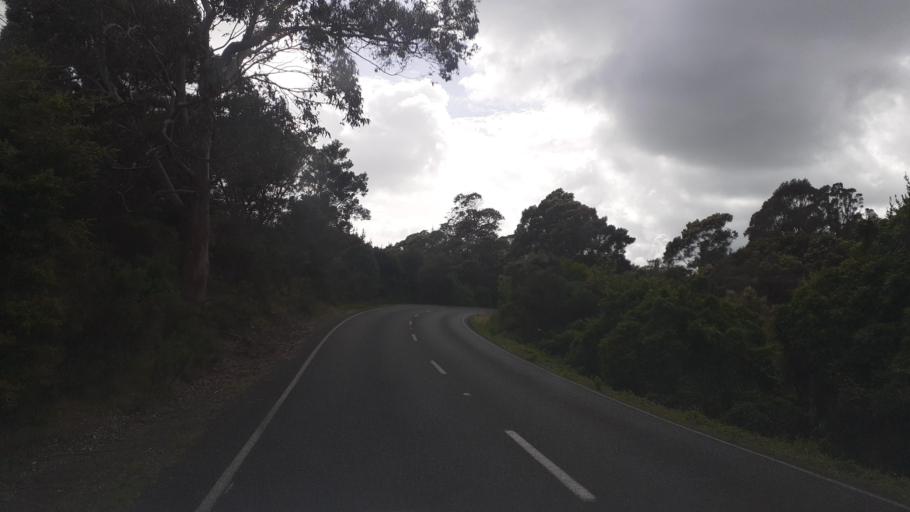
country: NZ
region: Northland
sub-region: Far North District
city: Kerikeri
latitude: -35.2253
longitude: 174.0104
